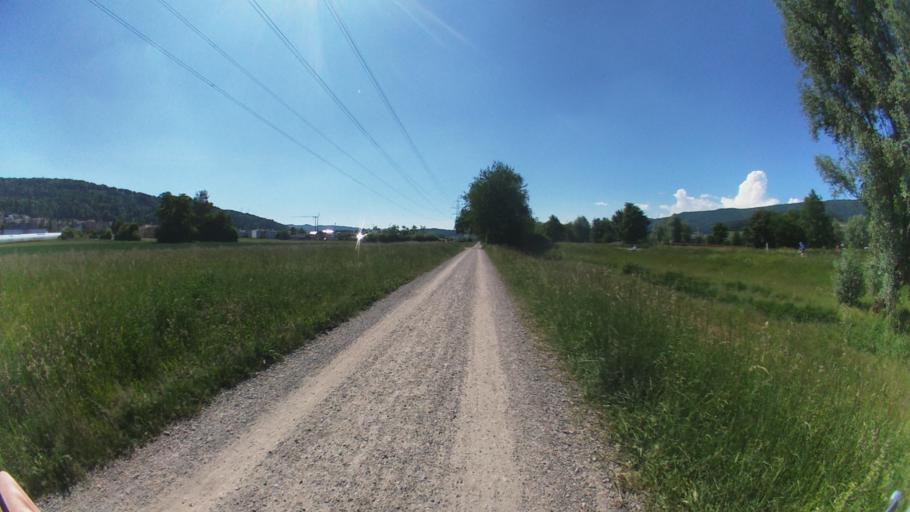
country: CH
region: Zurich
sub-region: Bezirk Dielsdorf
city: Daenikon
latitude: 47.4503
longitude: 8.4115
